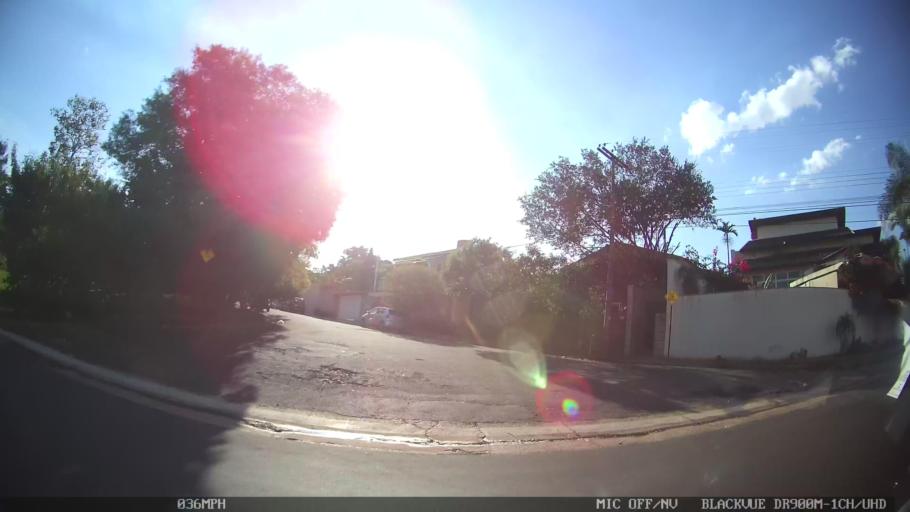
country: BR
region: Sao Paulo
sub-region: Ribeirao Preto
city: Ribeirao Preto
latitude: -21.2067
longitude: -47.7769
